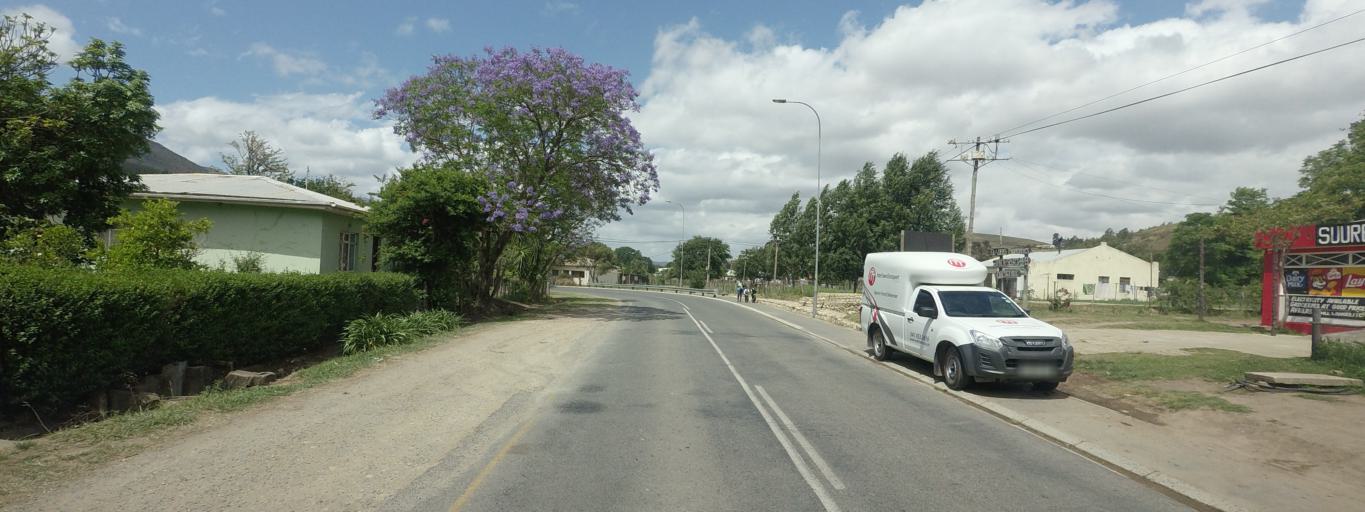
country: ZA
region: Western Cape
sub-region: Overberg District Municipality
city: Swellendam
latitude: -34.0034
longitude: 20.6472
